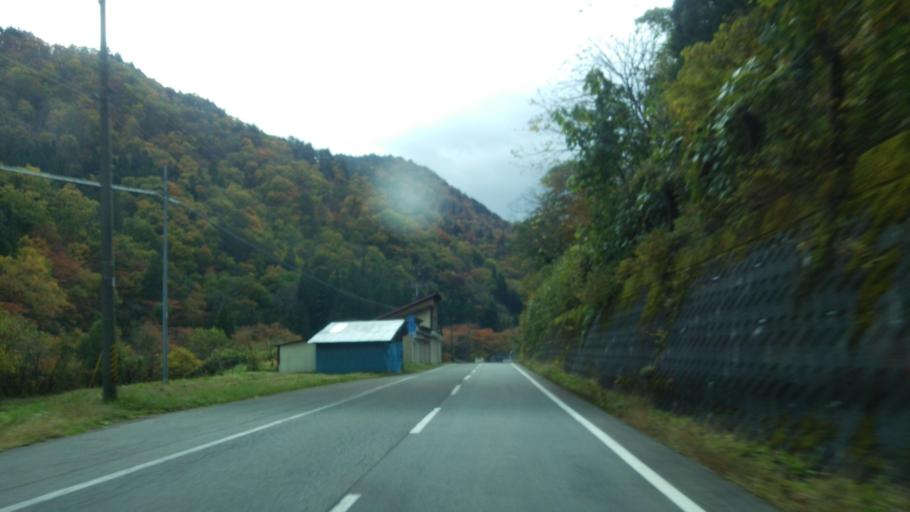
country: JP
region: Fukushima
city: Kitakata
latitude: 37.4181
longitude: 139.6972
